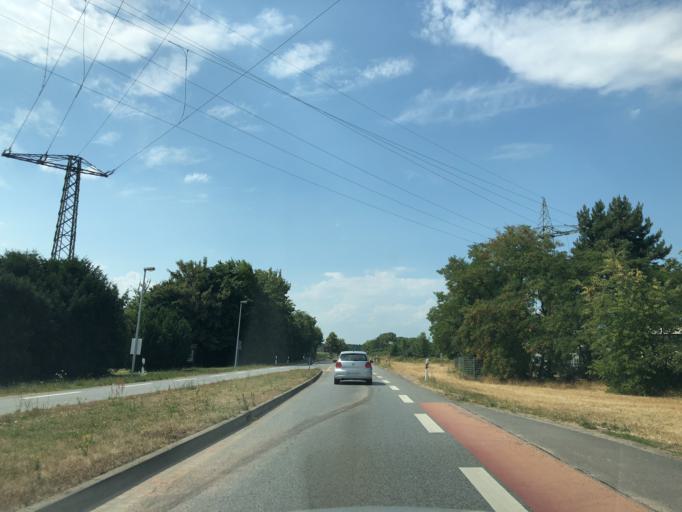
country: DE
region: Hesse
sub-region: Regierungsbezirk Darmstadt
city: Babenhausen
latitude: 49.9706
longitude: 8.9484
